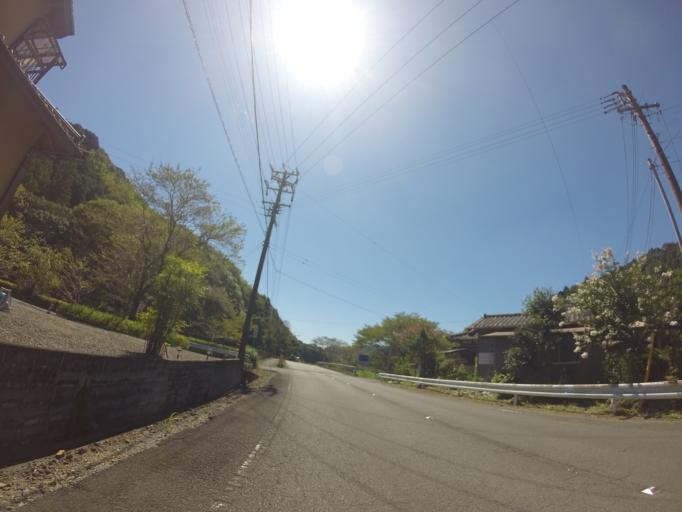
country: JP
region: Shizuoka
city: Fujieda
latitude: 34.9356
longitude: 138.2048
